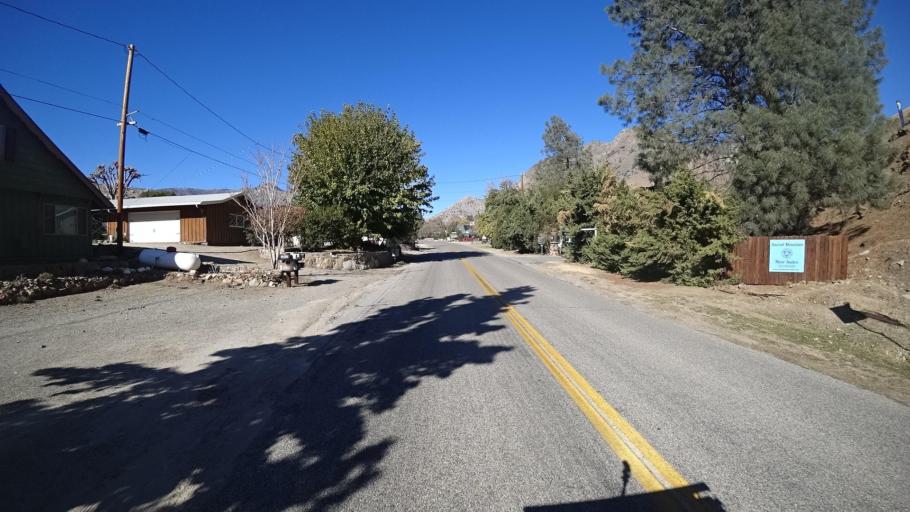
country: US
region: California
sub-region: Kern County
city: Kernville
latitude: 35.7859
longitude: -118.4464
